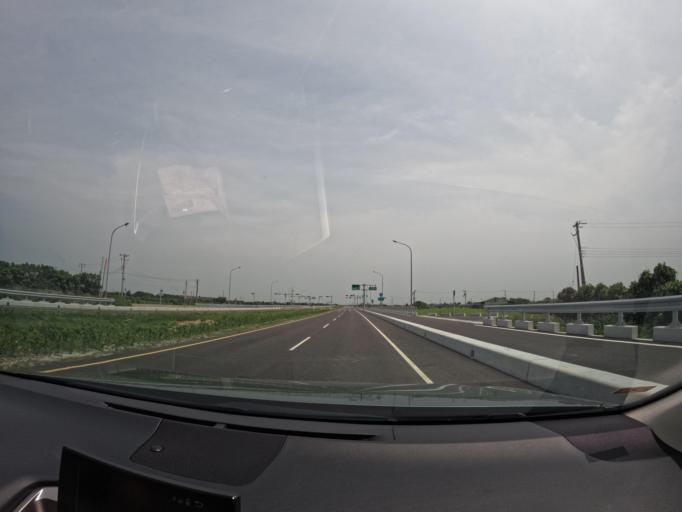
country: TW
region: Taiwan
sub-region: Changhua
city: Chang-hua
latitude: 23.9363
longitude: 120.3317
